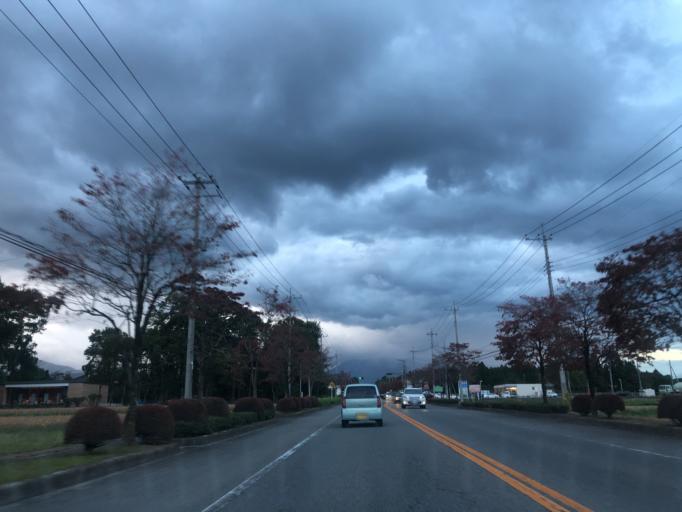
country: JP
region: Tochigi
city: Kuroiso
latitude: 36.9465
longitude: 140.0063
